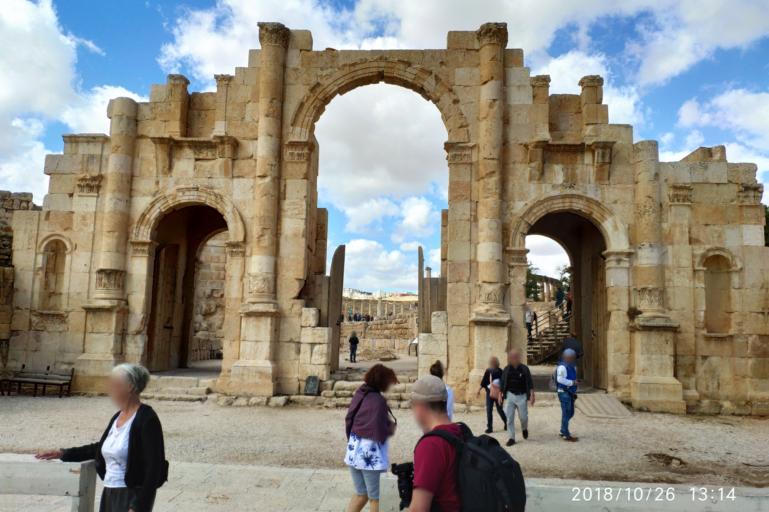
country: JO
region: Jerash
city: Jarash
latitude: 32.2763
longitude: 35.8911
